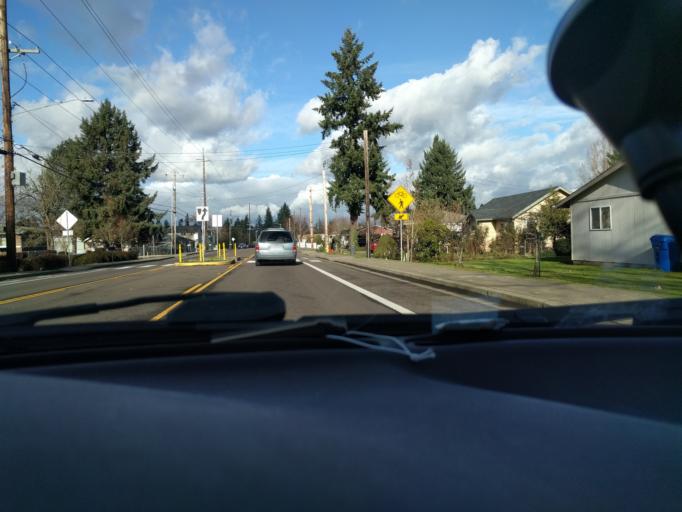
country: US
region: Oregon
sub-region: Marion County
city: Hayesville
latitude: 44.9726
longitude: -122.9916
